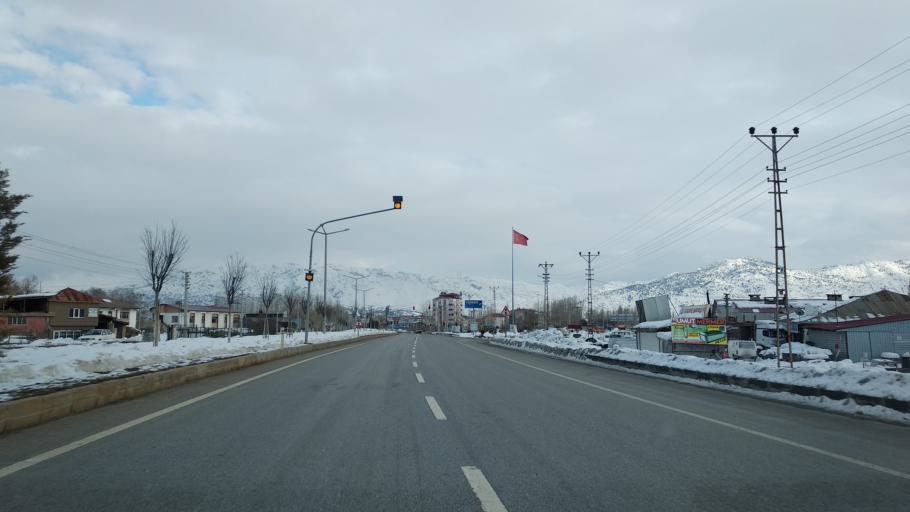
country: TR
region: Kahramanmaras
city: Goksun
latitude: 38.0301
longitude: 36.4784
